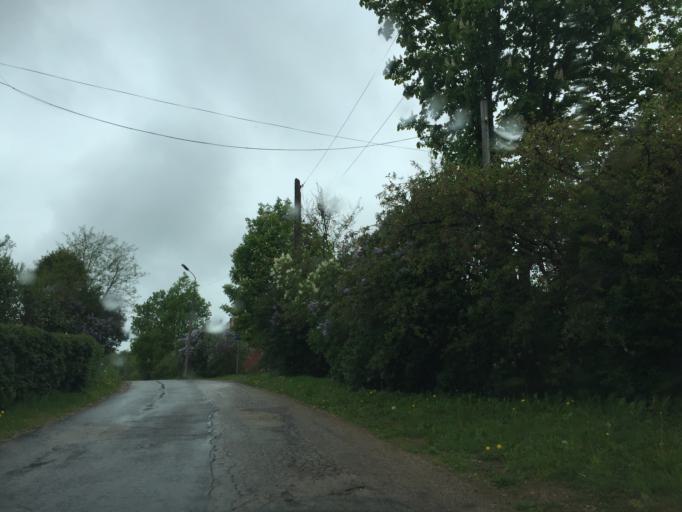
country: LV
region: Lielvarde
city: Lielvarde
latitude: 56.7215
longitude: 24.7928
